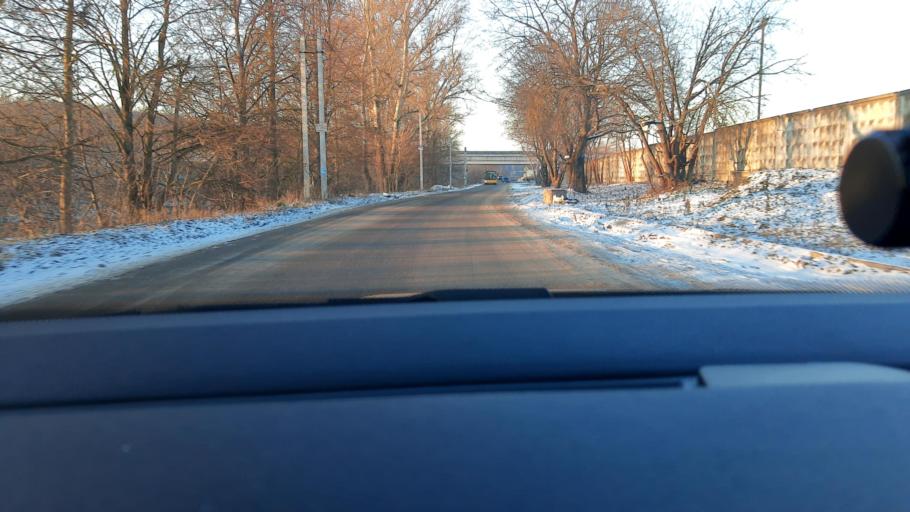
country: RU
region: Moskovskaya
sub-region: Leninskiy Rayon
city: Molokovo
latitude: 55.4945
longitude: 37.8483
